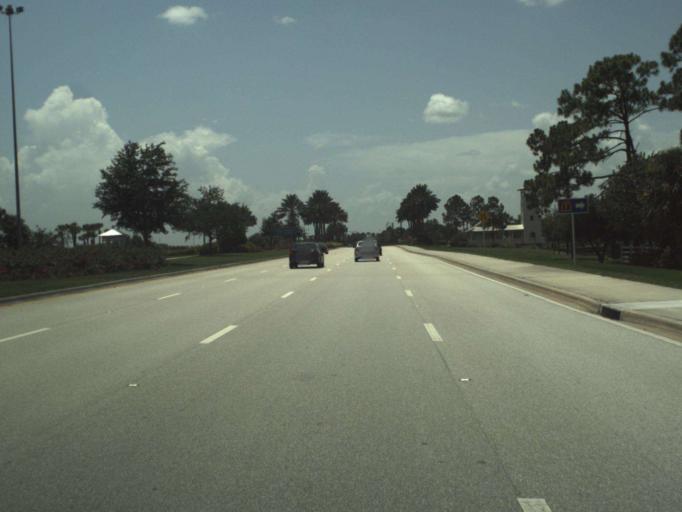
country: US
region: Florida
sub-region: Saint Lucie County
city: Port Saint Lucie
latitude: 27.2645
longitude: -80.4261
